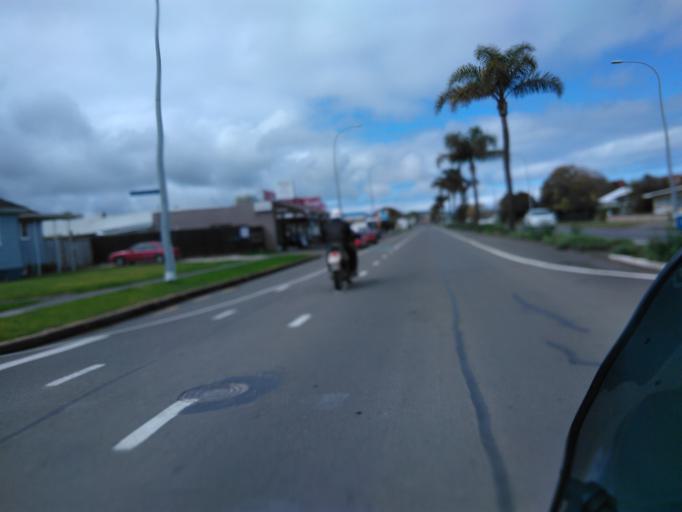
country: NZ
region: Gisborne
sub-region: Gisborne District
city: Gisborne
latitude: -38.6535
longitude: 178.0029
